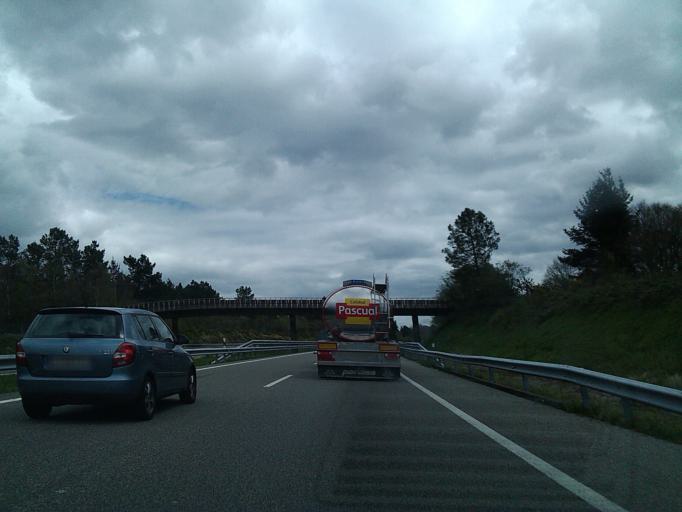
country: ES
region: Galicia
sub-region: Provincia de Lugo
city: Guitiriz
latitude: 43.1928
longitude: -7.8764
